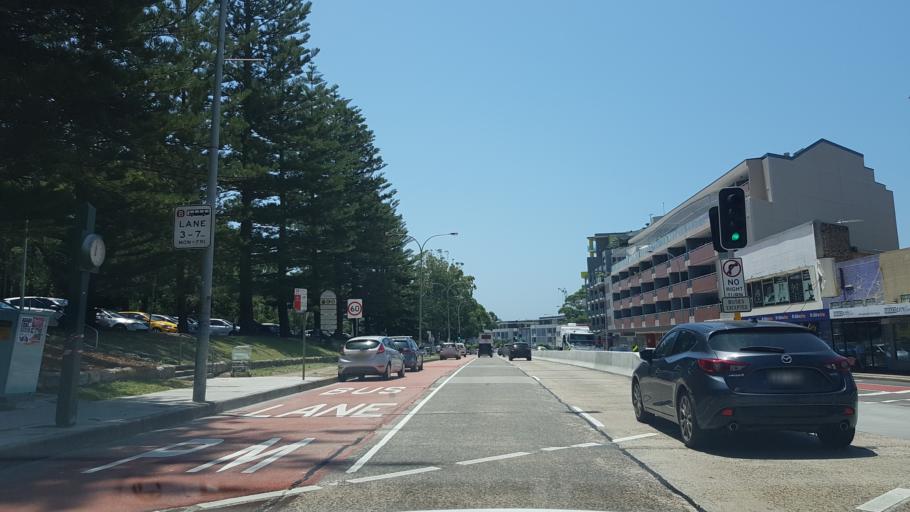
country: AU
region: New South Wales
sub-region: Warringah
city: North Curl Curl
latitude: -33.7525
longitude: 151.2868
